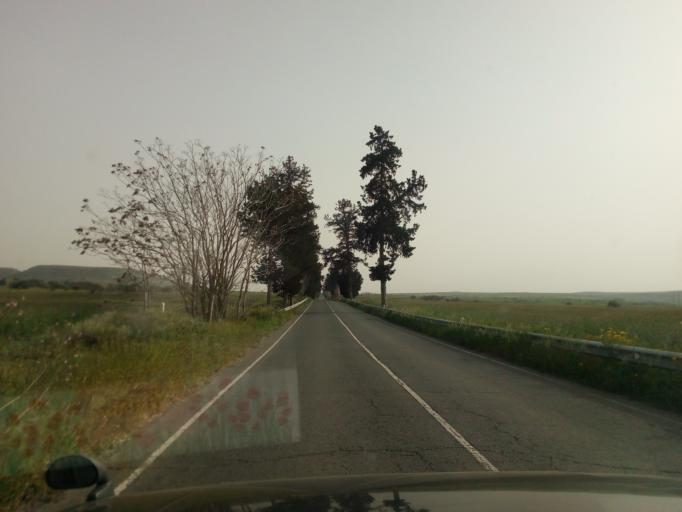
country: CY
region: Lefkosia
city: Lympia
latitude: 35.0288
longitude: 33.4929
